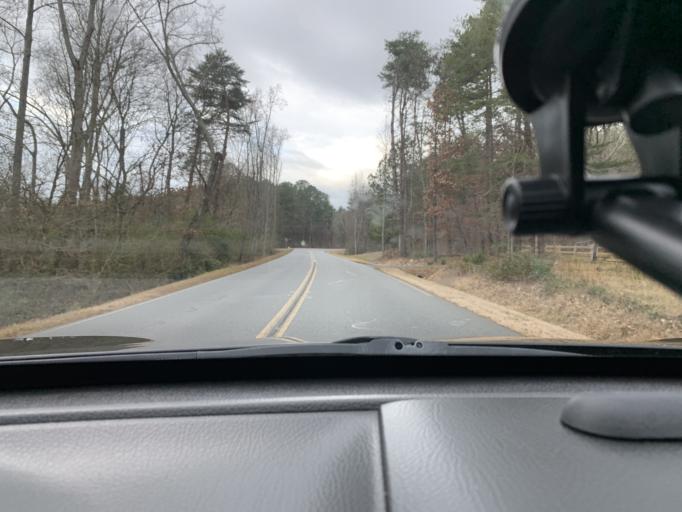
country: US
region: Georgia
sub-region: Bartow County
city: Rydal
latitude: 34.3484
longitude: -84.6784
